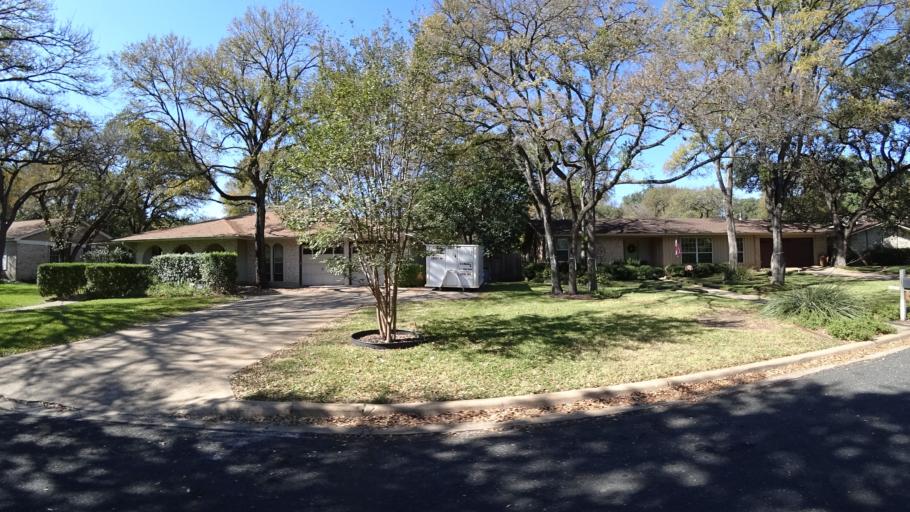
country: US
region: Texas
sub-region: Williamson County
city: Jollyville
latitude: 30.3776
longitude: -97.7439
